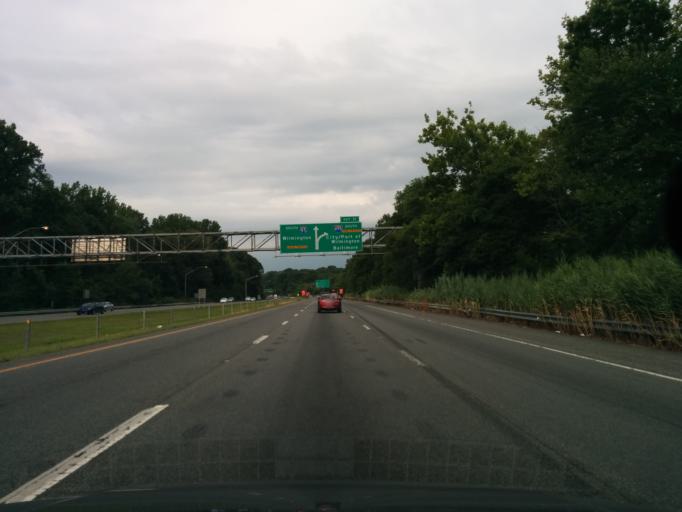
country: US
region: Pennsylvania
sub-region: Delaware County
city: Boothwyn
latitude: 39.8235
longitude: -75.4412
